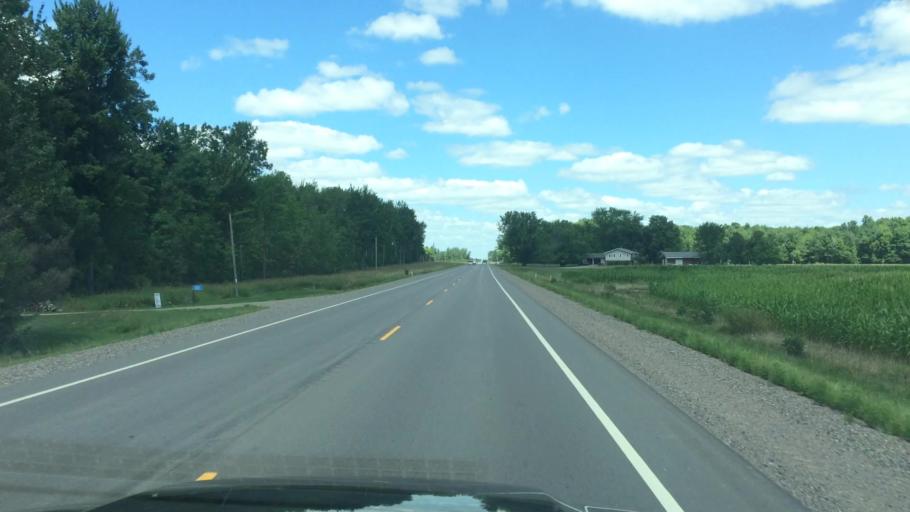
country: US
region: Wisconsin
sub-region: Clark County
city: Abbotsford
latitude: 45.0218
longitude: -90.3151
